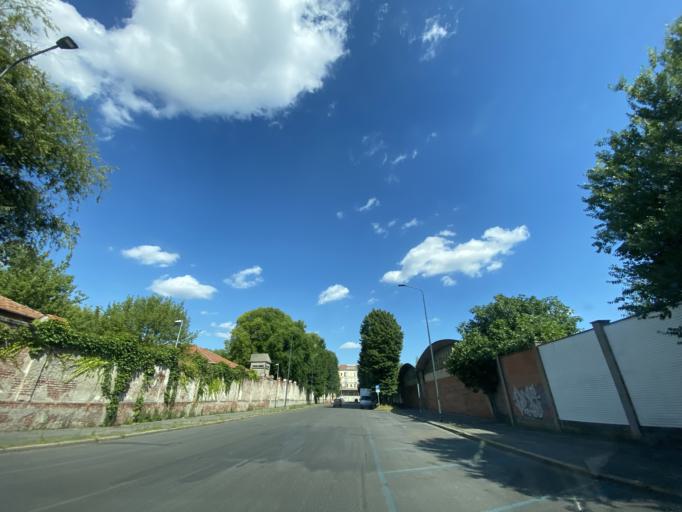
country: IT
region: Lombardy
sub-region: Citta metropolitana di Milano
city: Bresso
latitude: 45.5138
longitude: 9.1993
